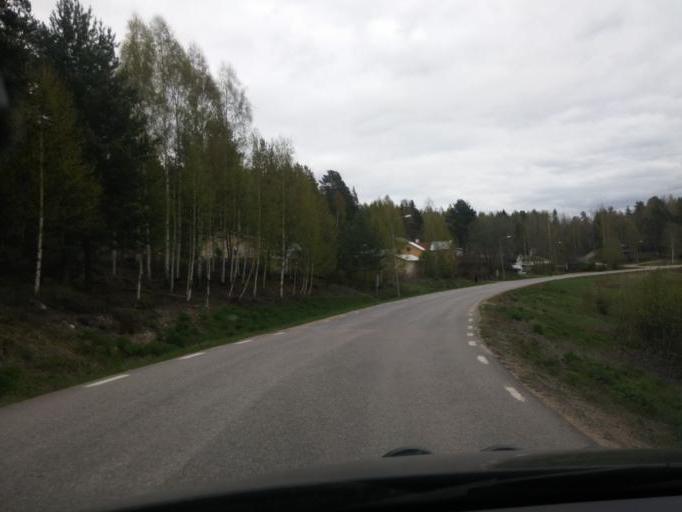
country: SE
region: Gaevleborg
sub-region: Ljusdals Kommun
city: Ljusdal
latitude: 61.8559
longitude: 16.0372
